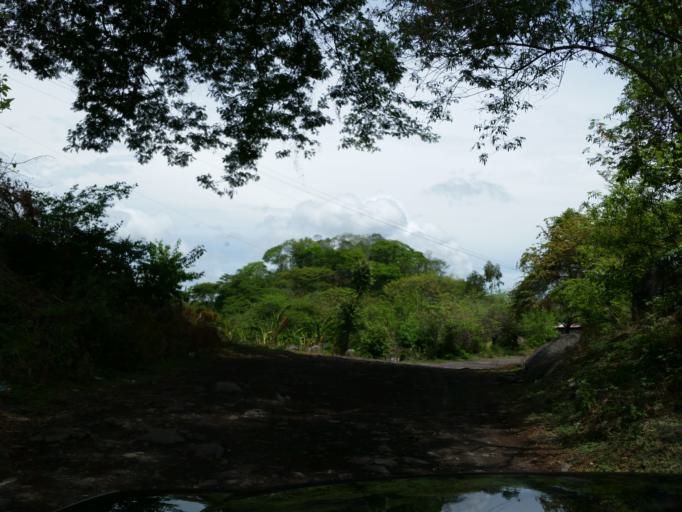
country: NI
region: Granada
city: Granada
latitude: 11.9060
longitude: -85.9080
